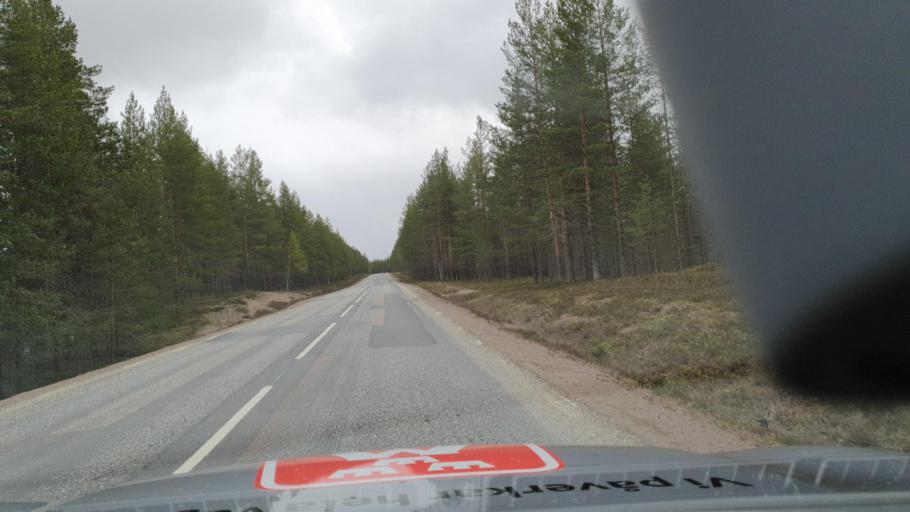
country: SE
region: Vaesternorrland
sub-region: Solleftea Kommun
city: Solleftea
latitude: 63.6453
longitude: 17.3922
